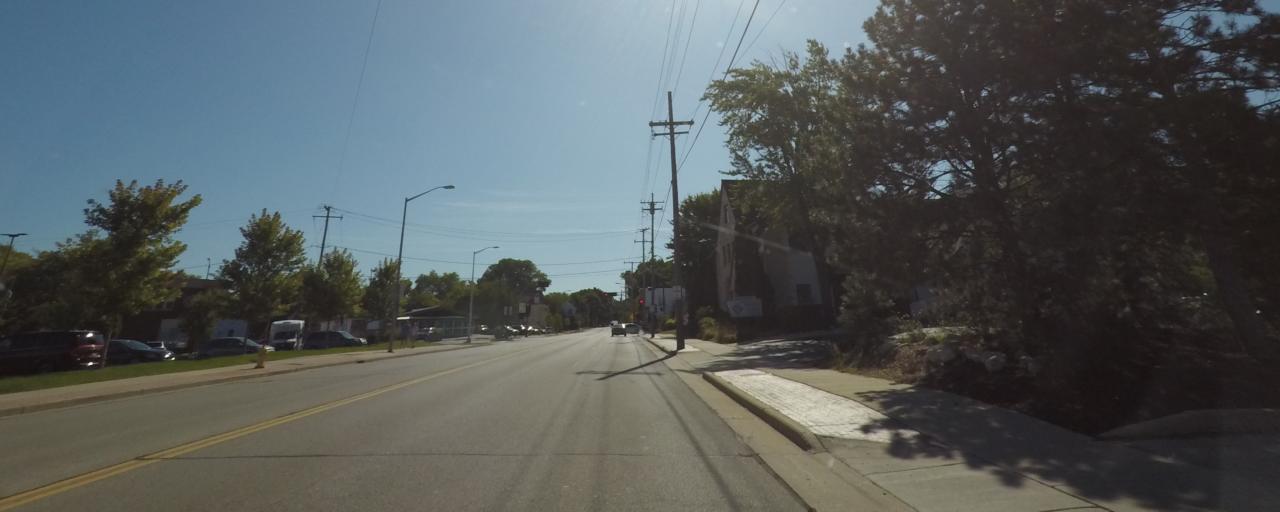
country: US
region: Wisconsin
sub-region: Waukesha County
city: Waukesha
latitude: 43.0082
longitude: -88.2228
